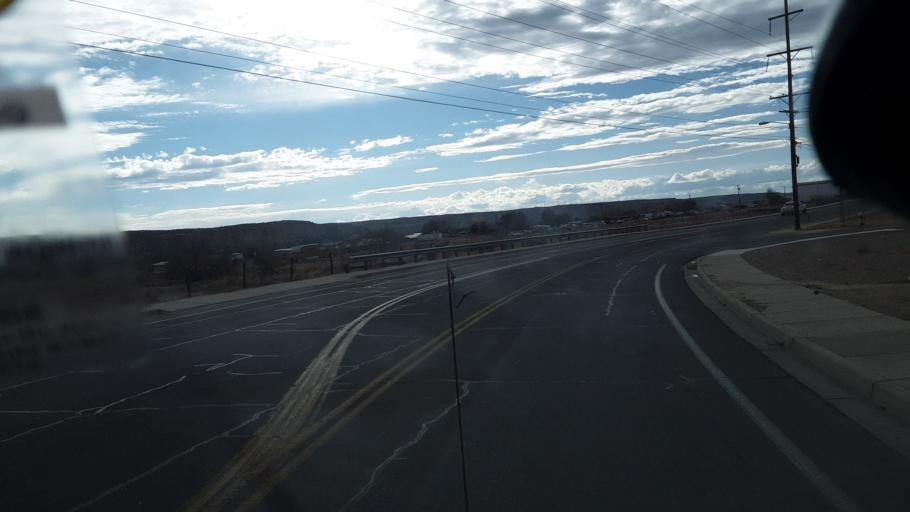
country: US
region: New Mexico
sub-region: San Juan County
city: Farmington
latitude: 36.7267
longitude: -108.1614
